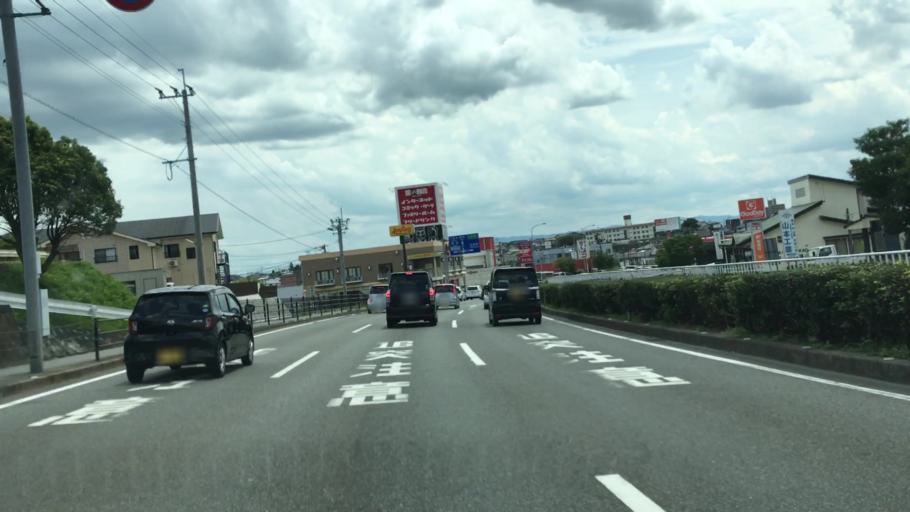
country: JP
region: Fukuoka
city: Chikushino-shi
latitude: 33.4966
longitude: 130.5343
